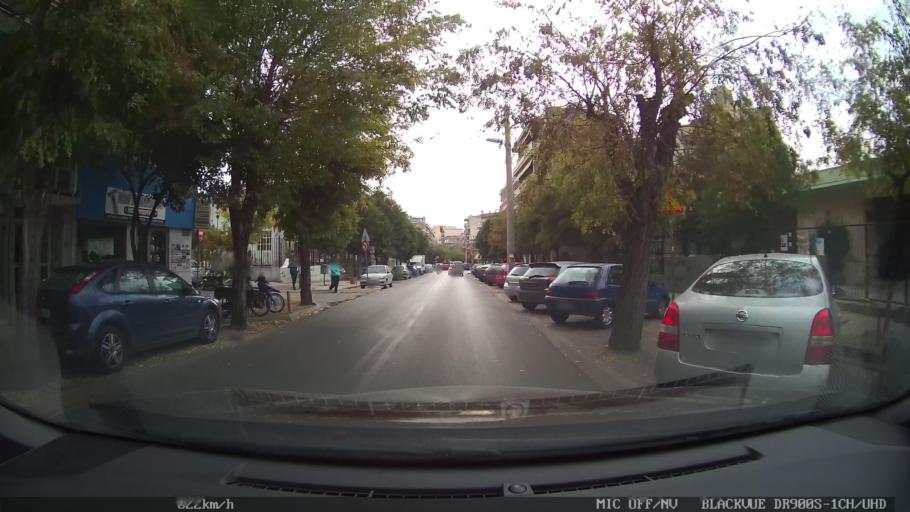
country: GR
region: Central Macedonia
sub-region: Nomos Thessalonikis
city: Triandria
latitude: 40.6086
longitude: 22.9754
